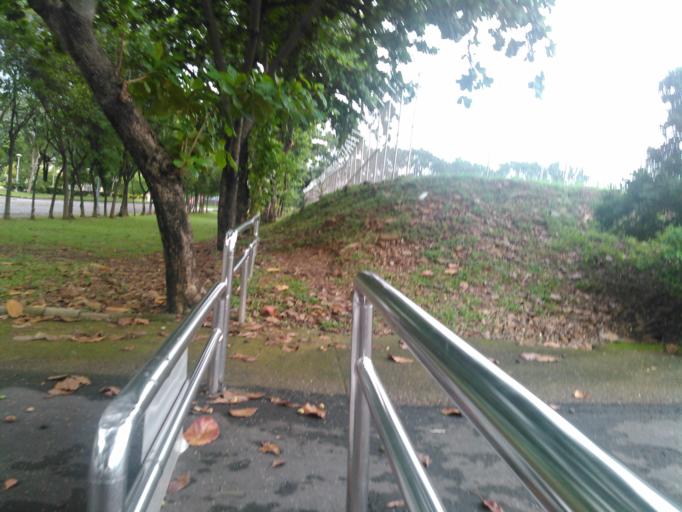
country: TW
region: Taiwan
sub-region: Pingtung
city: Pingtung
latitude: 22.6469
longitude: 120.6131
